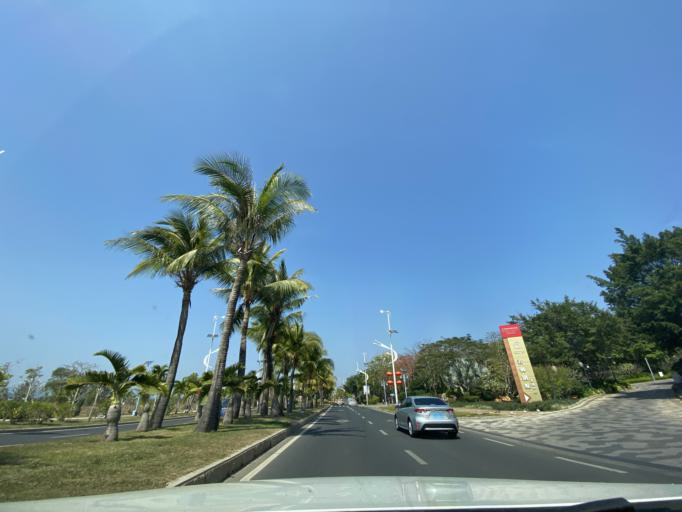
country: CN
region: Hainan
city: Haitangwan
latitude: 18.3467
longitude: 109.7332
